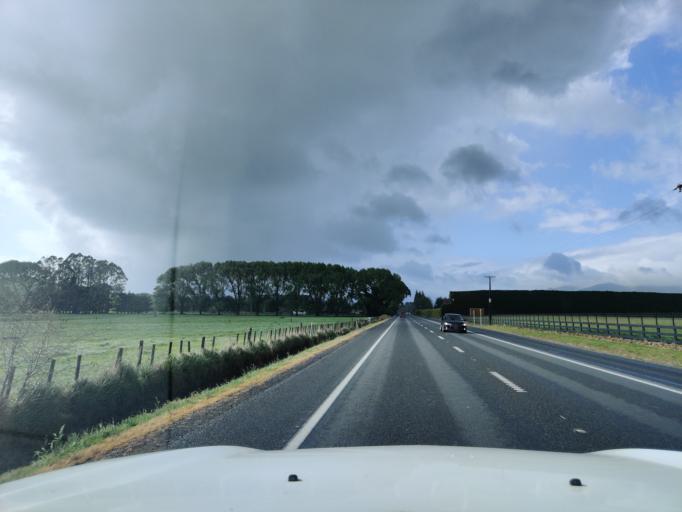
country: NZ
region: Waikato
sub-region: Waipa District
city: Cambridge
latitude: -37.9323
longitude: 175.5728
